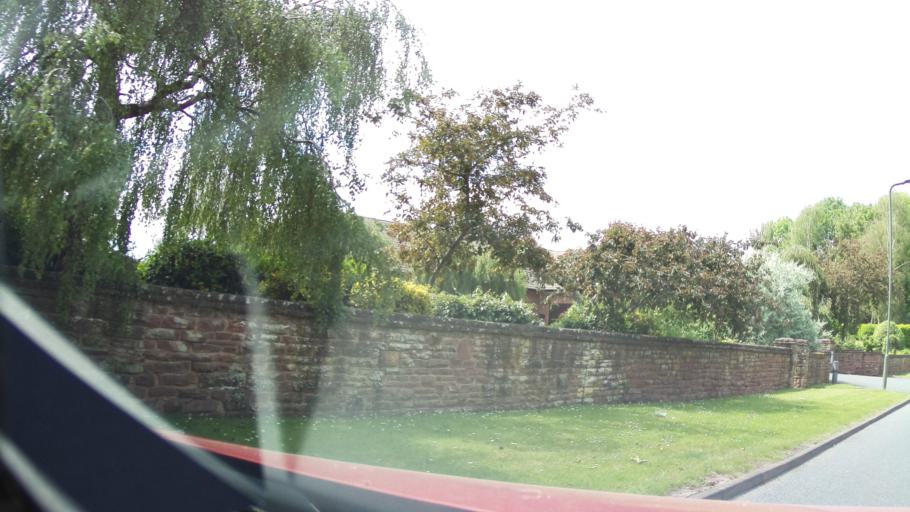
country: GB
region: England
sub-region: Herefordshire
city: Ross on Wye
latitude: 51.9202
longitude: -2.5879
